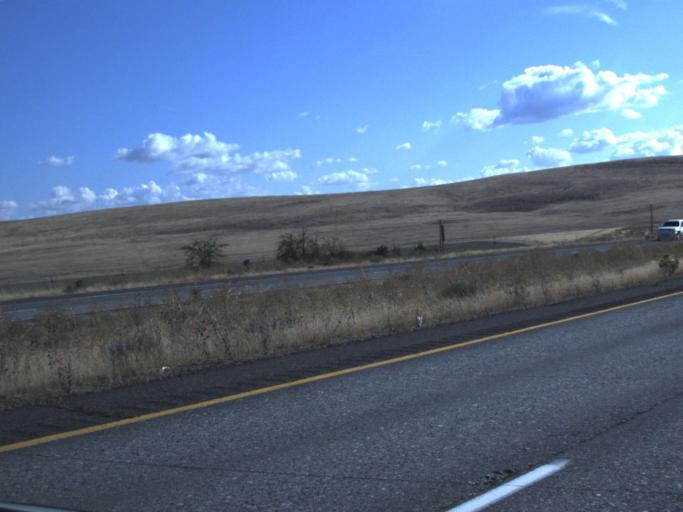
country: US
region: Oregon
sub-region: Umatilla County
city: Umatilla
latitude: 46.0196
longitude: -119.2260
